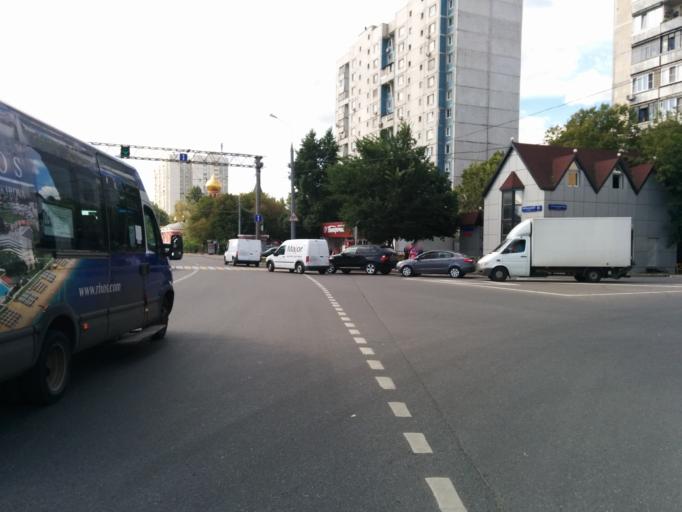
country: RU
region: Moscow
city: Mar'ina Roshcha
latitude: 55.8072
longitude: 37.6156
